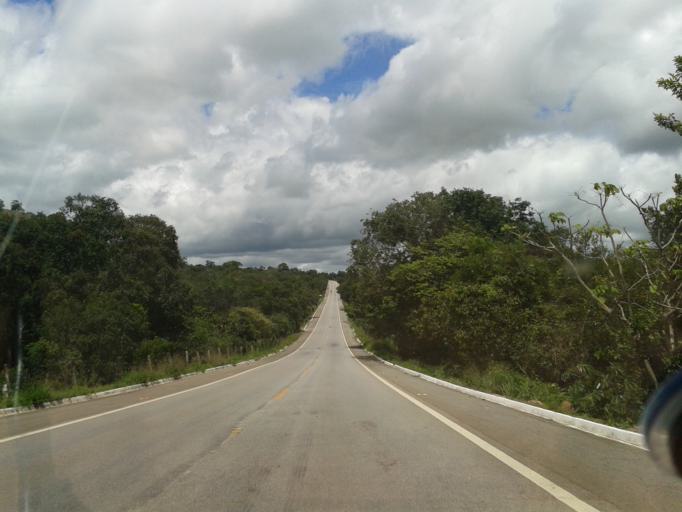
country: BR
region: Goias
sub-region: Goias
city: Goias
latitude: -15.8739
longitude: -50.0941
